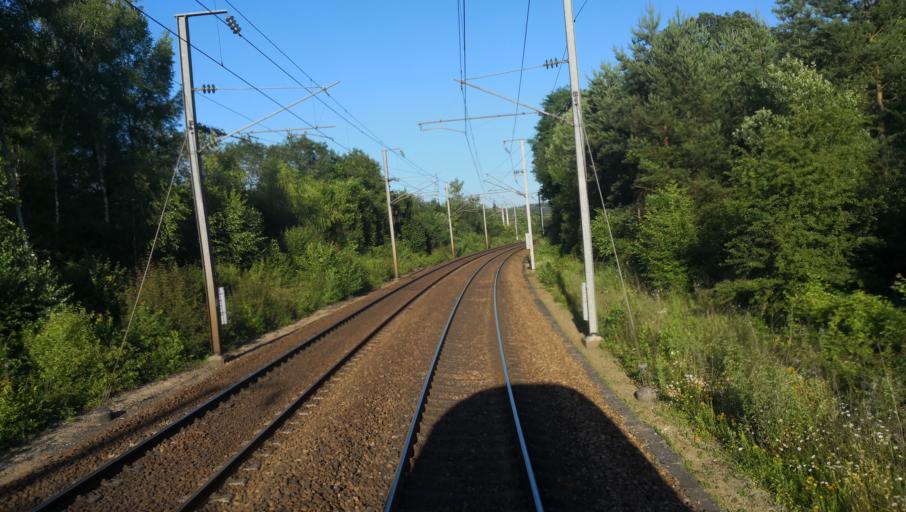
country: FR
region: Haute-Normandie
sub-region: Departement de l'Eure
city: Serquigny
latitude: 49.1082
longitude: 0.7272
